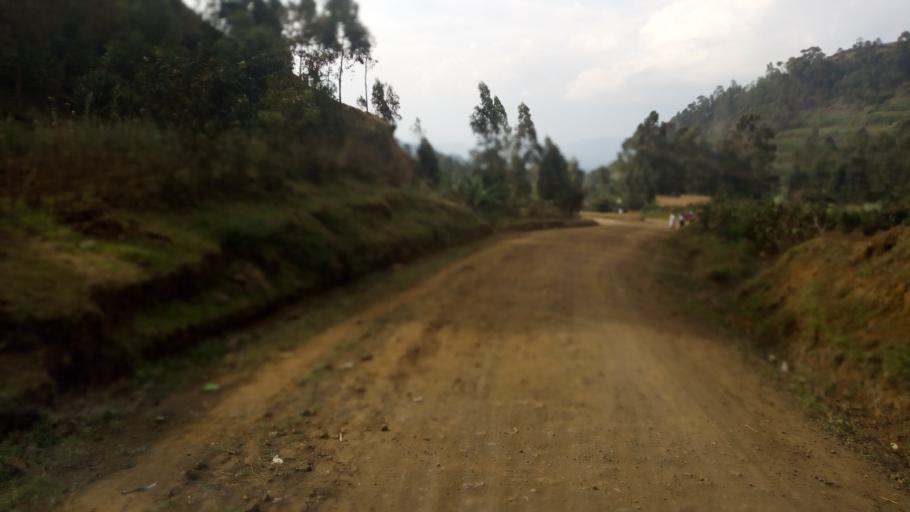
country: UG
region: Western Region
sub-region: Kisoro District
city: Kisoro
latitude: -1.2990
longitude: 29.7021
